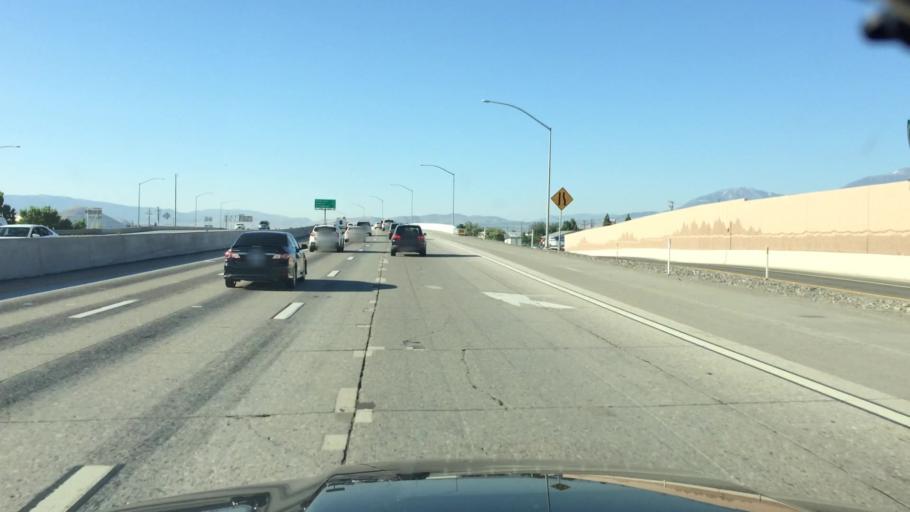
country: US
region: Nevada
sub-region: Washoe County
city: Reno
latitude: 39.5223
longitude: -119.7838
